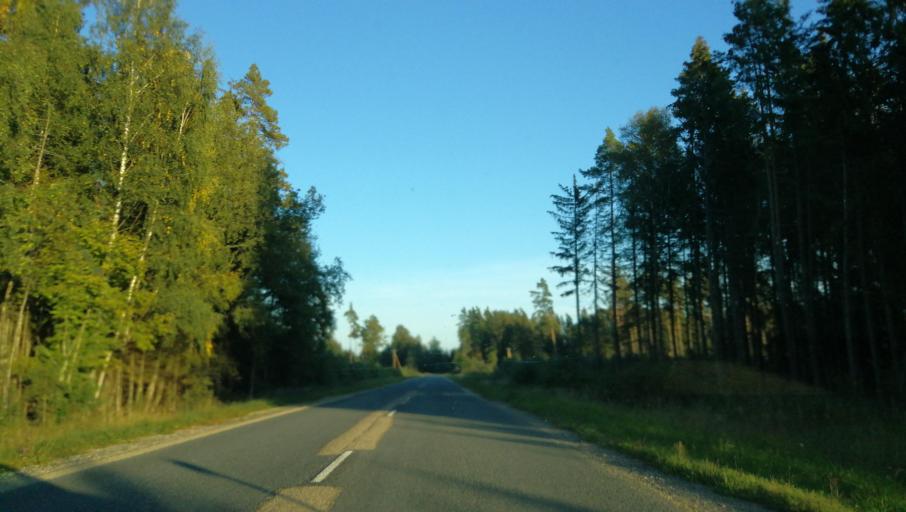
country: LV
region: Aizpute
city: Aizpute
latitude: 56.6239
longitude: 21.7126
